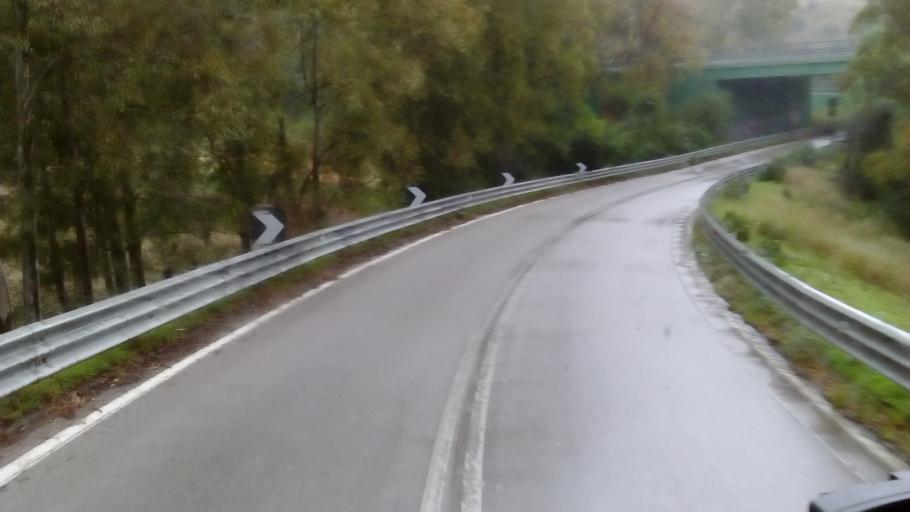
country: IT
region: Sicily
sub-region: Enna
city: Pietraperzia
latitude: 37.4921
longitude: 14.1483
